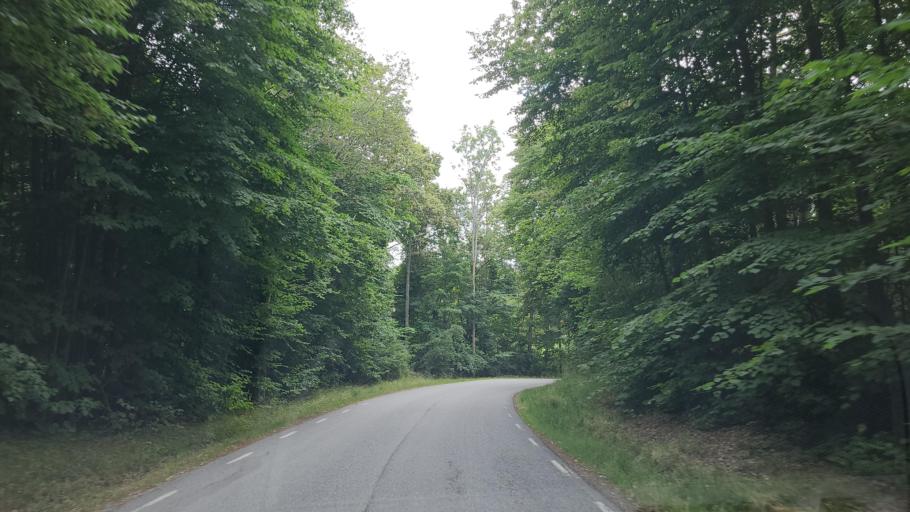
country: SE
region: Stockholm
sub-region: Upplands-Bro Kommun
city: Bro
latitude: 59.4697
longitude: 17.5928
